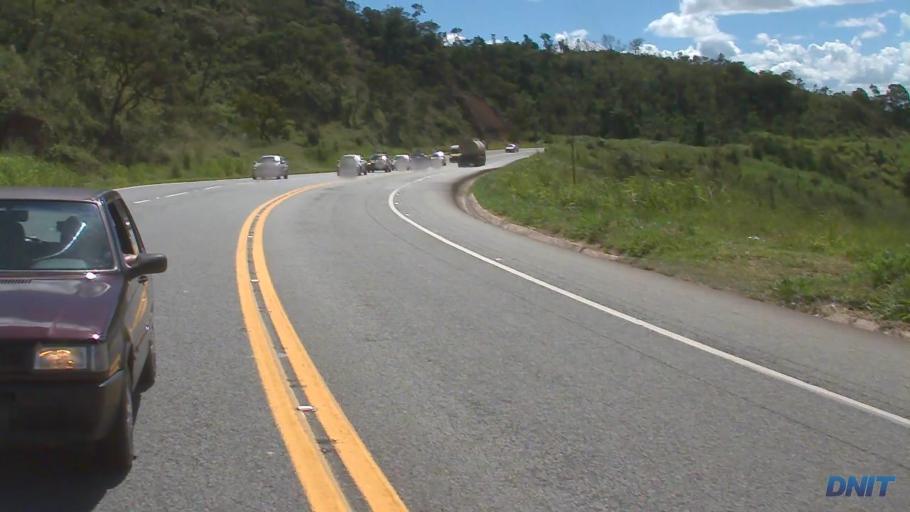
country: BR
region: Minas Gerais
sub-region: Caete
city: Caete
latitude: -19.7869
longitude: -43.7160
